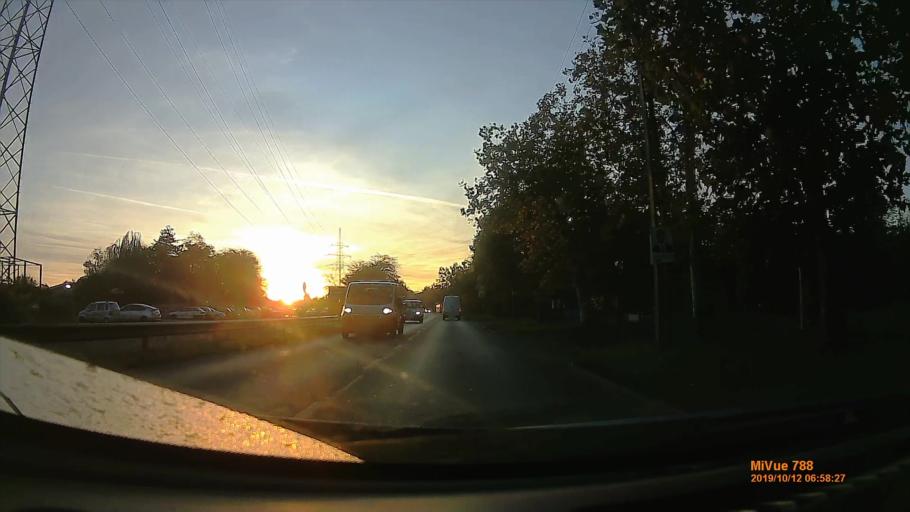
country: HU
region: Hajdu-Bihar
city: Debrecen
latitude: 47.5228
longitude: 21.6474
